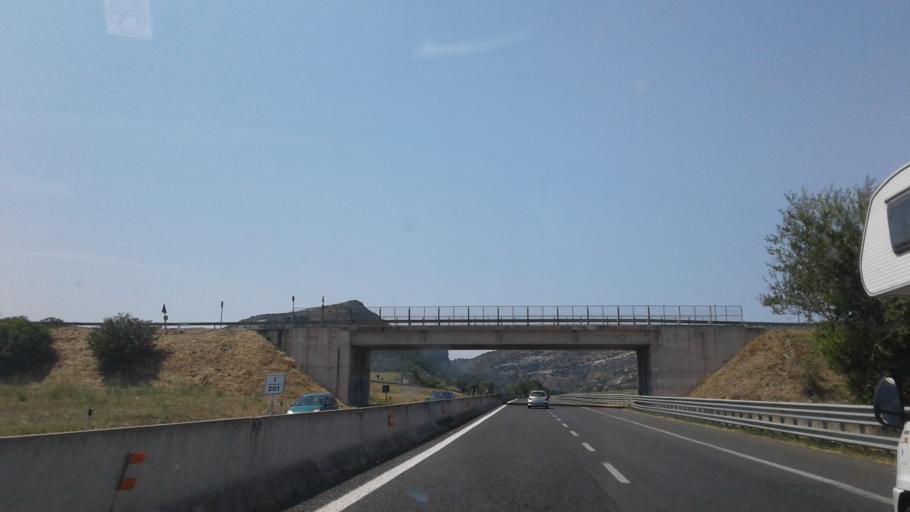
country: IT
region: Sardinia
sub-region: Provincia di Sassari
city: Muros
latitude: 40.6862
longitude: 8.6306
